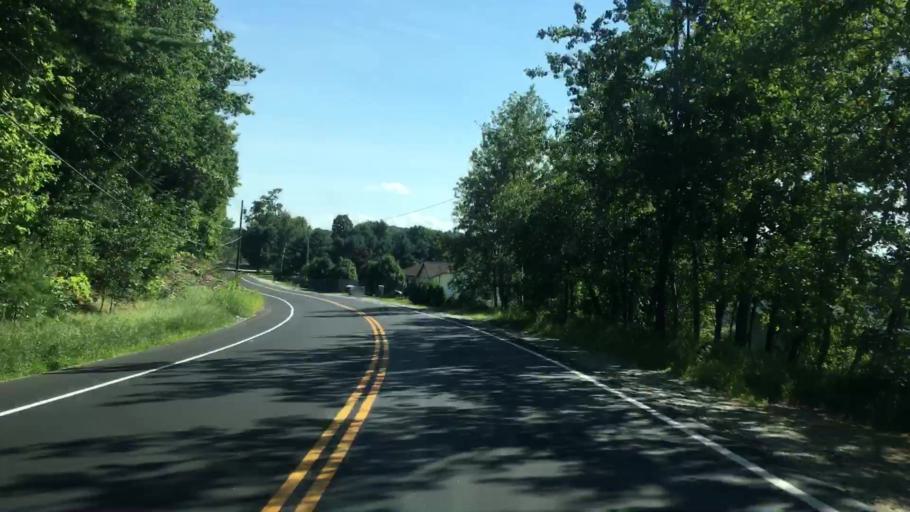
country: US
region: Maine
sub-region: Androscoggin County
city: Sabattus
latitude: 44.1314
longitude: -70.0877
